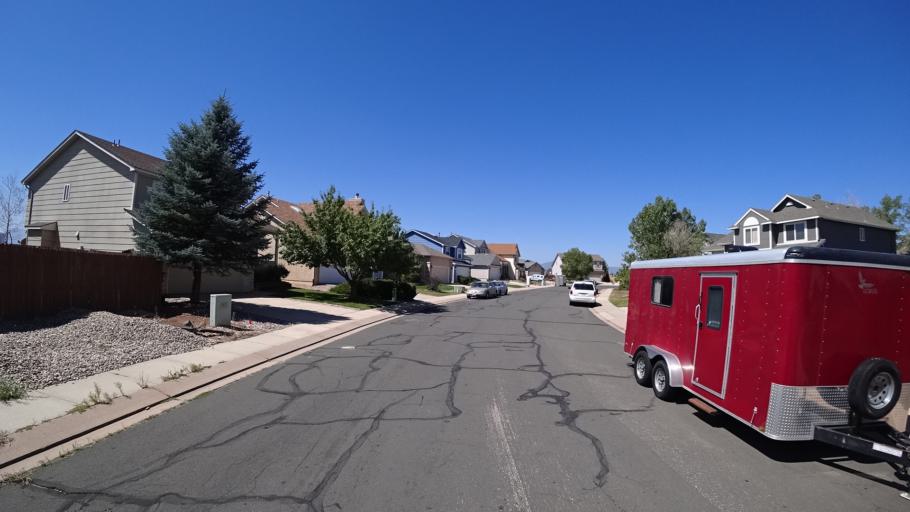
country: US
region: Colorado
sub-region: El Paso County
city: Black Forest
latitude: 38.9500
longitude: -104.7596
